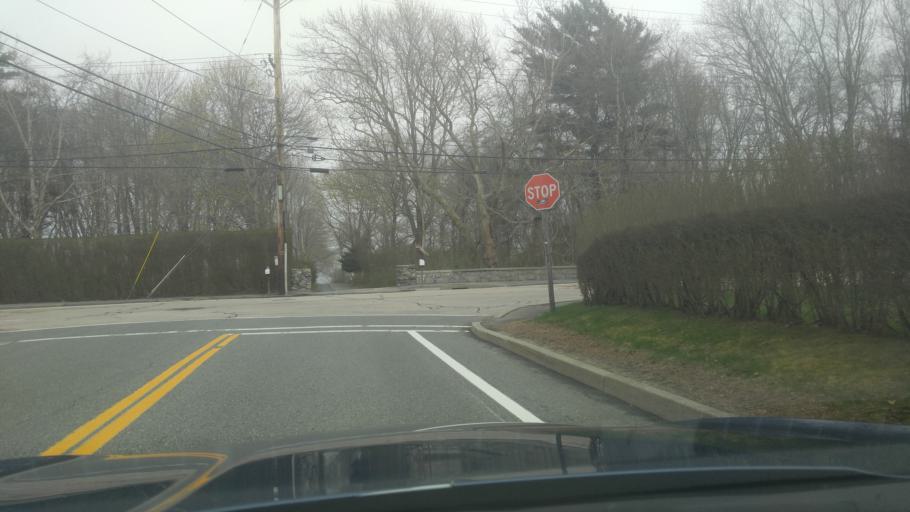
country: US
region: Rhode Island
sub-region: Newport County
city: Jamestown
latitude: 41.4891
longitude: -71.3674
